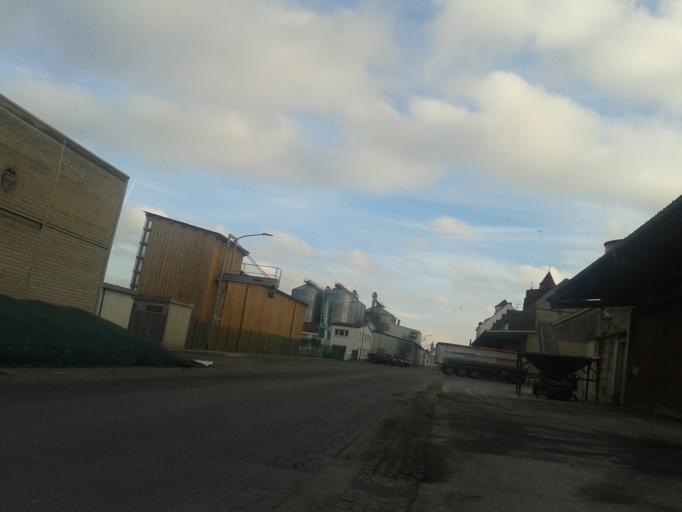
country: DE
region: Bavaria
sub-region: Upper Franconia
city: Hallstadt
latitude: 49.9084
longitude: 10.8712
